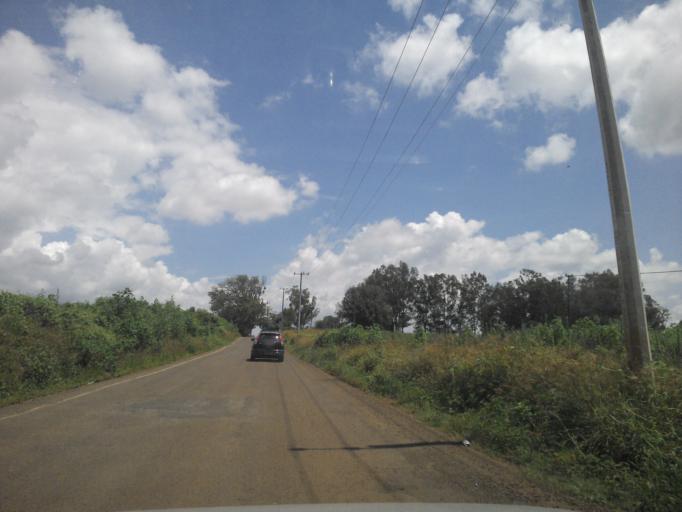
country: MX
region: Jalisco
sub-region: Atotonilco el Alto
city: Ojo de Agua de Moran
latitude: 20.6024
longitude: -102.4815
